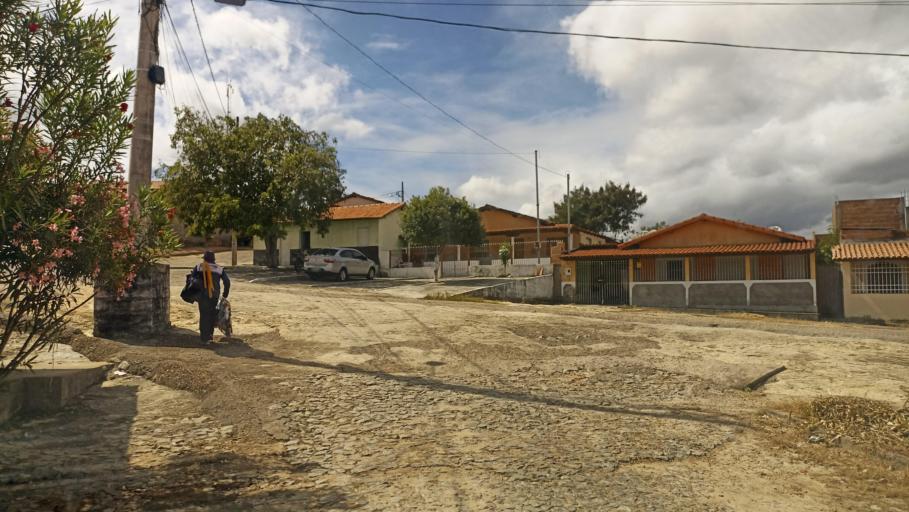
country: BR
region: Minas Gerais
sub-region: Jequitinhonha
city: Jequitinhonha
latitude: -16.4365
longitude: -41.0105
